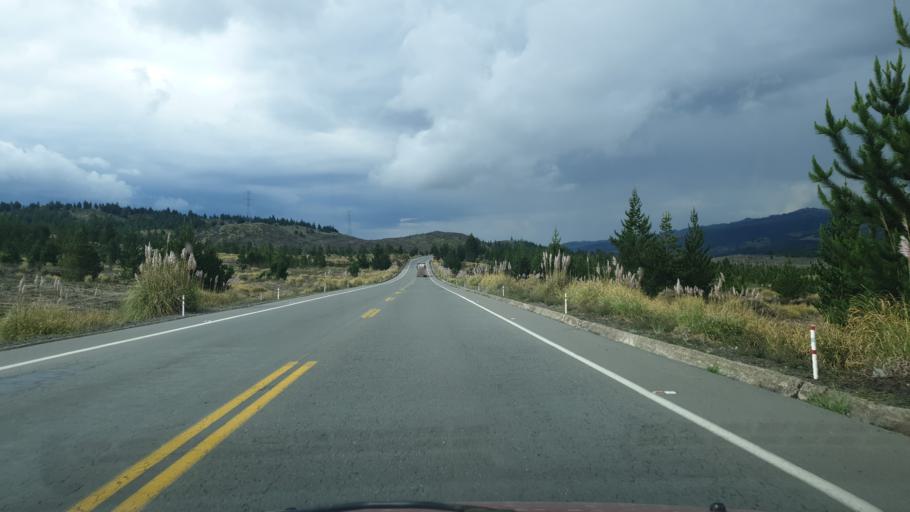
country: EC
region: Chimborazo
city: Alausi
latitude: -2.0529
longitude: -78.7431
